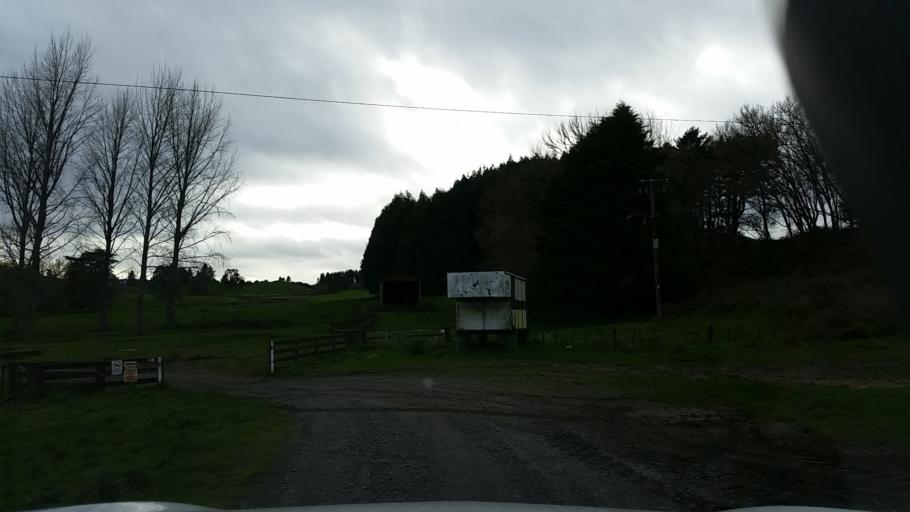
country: NZ
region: Bay of Plenty
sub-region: Rotorua District
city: Rotorua
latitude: -38.2989
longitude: 176.4224
